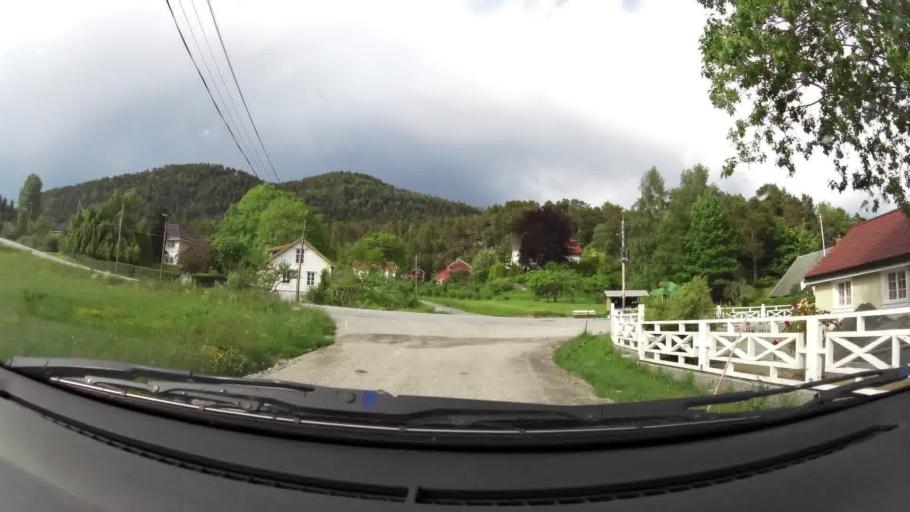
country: NO
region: More og Romsdal
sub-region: Kristiansund
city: Kristiansund
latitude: 63.0294
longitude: 7.7515
